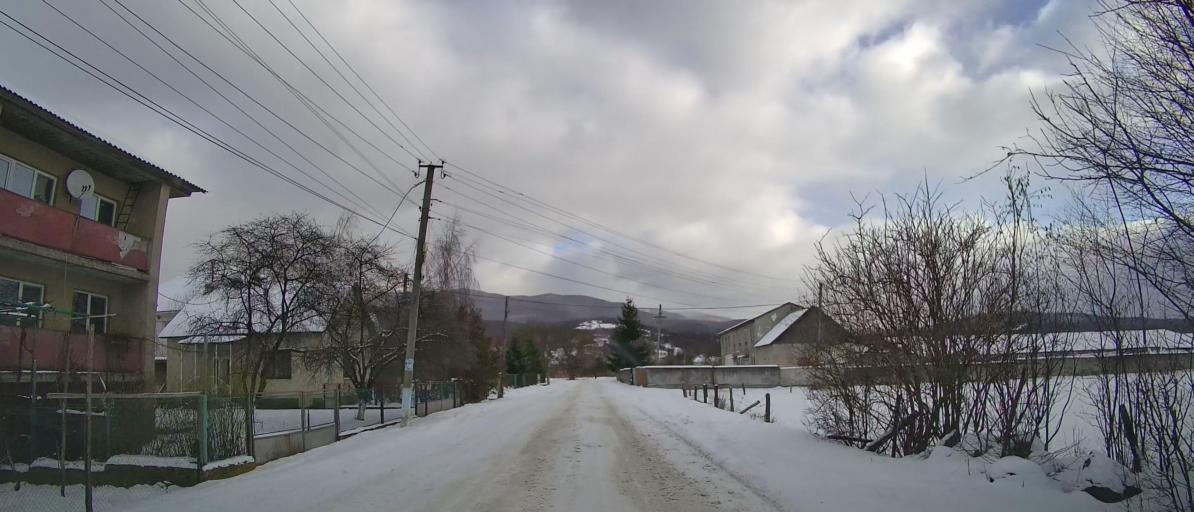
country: UA
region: Zakarpattia
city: Velykyi Bereznyi
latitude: 48.9238
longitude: 22.4590
